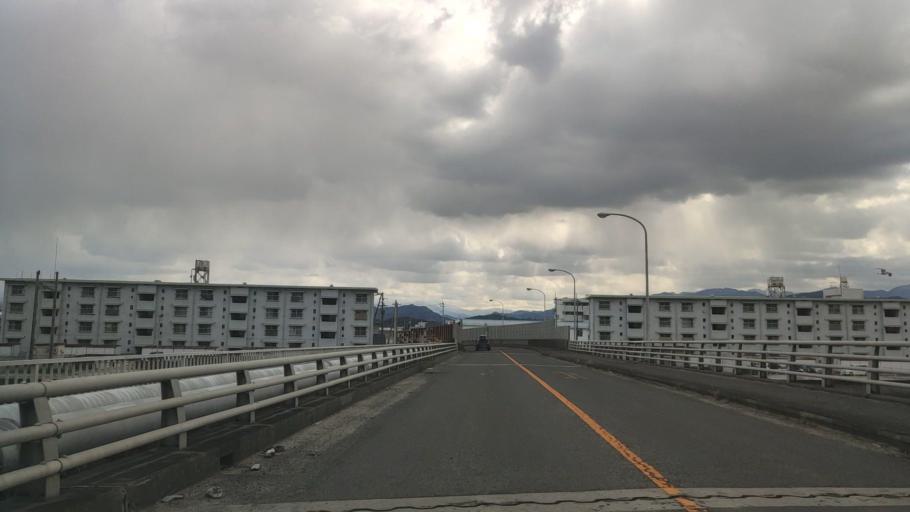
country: JP
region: Ehime
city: Saijo
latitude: 34.0594
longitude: 133.0175
